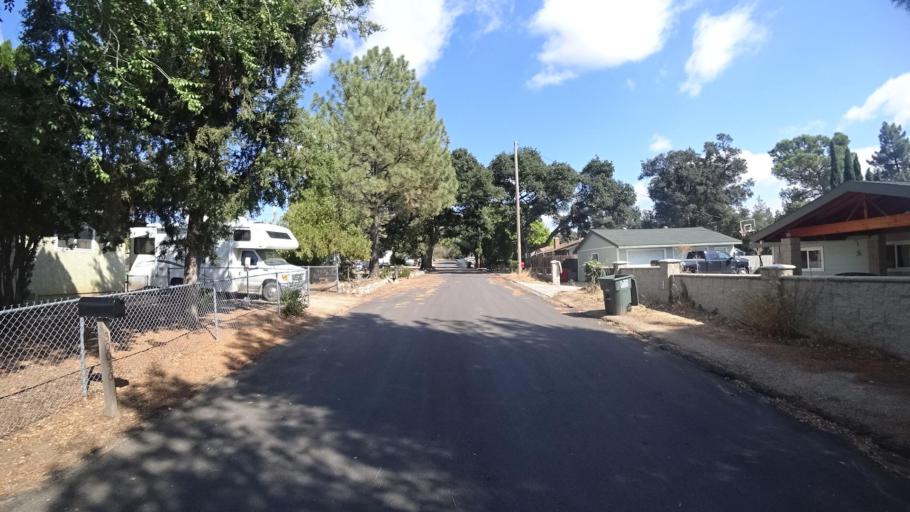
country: US
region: California
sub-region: San Diego County
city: Campo
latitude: 32.6818
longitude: -116.5049
